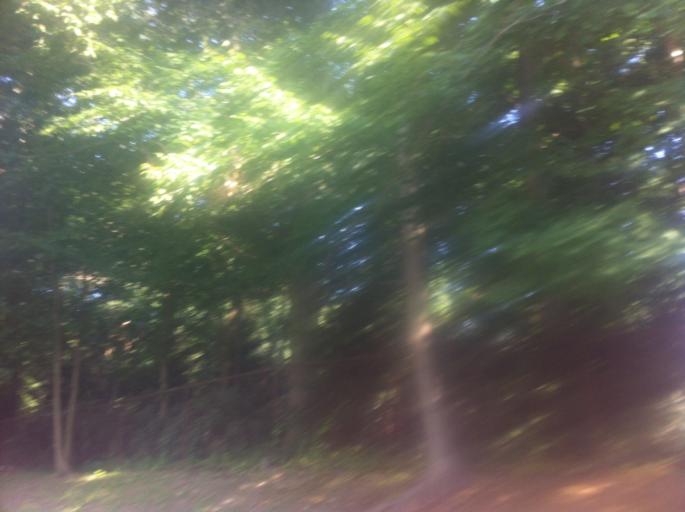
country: US
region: New York
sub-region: Nassau County
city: Locust Valley
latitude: 40.8554
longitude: -73.5919
